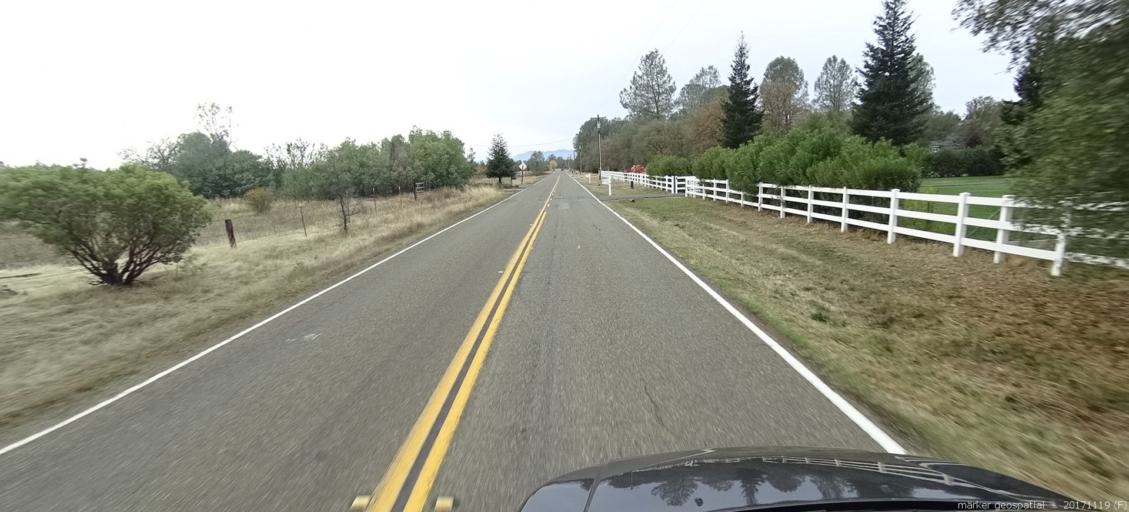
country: US
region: California
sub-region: Shasta County
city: Redding
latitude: 40.4882
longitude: -122.4278
